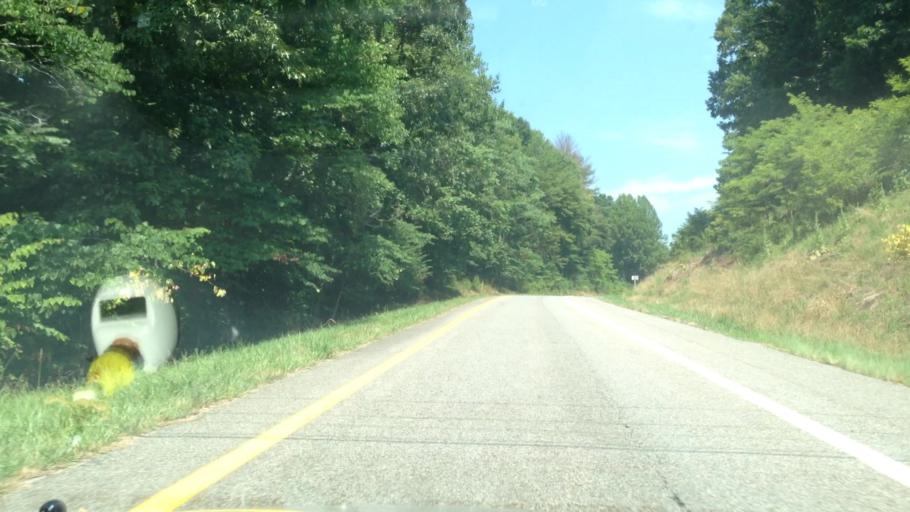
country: US
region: Virginia
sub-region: Henry County
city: Collinsville
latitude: 36.6941
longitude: -79.9508
